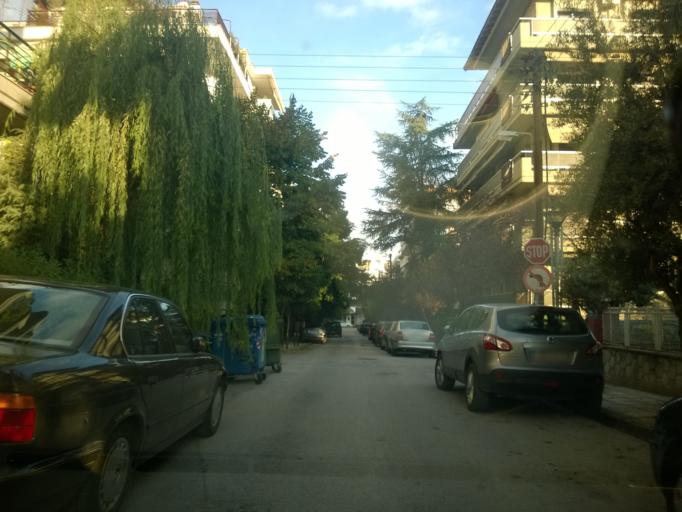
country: GR
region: Central Macedonia
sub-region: Nomos Thessalonikis
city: Kalamaria
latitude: 40.5868
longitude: 22.9581
